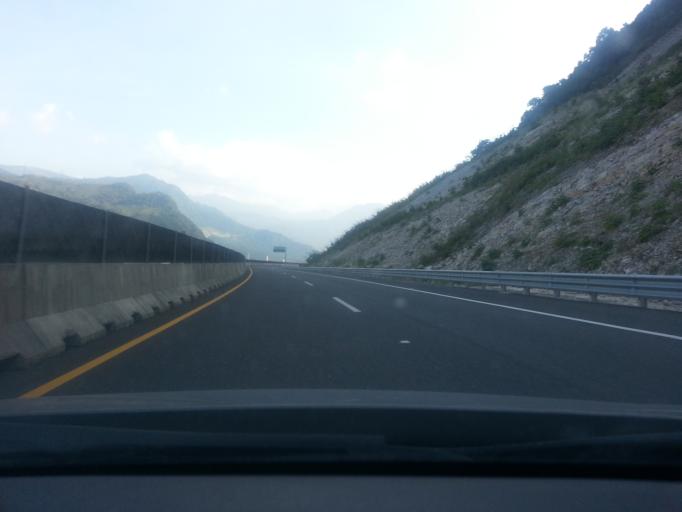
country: MX
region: Puebla
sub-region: Xicotepec
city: San Lorenzo
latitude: 20.3733
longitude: -97.9485
